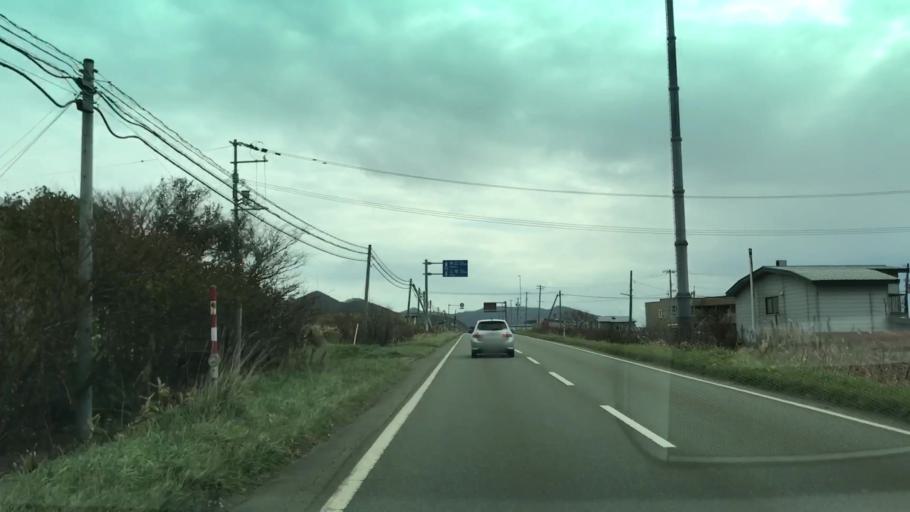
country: JP
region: Hokkaido
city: Shizunai-furukawacho
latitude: 42.0285
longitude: 143.1354
